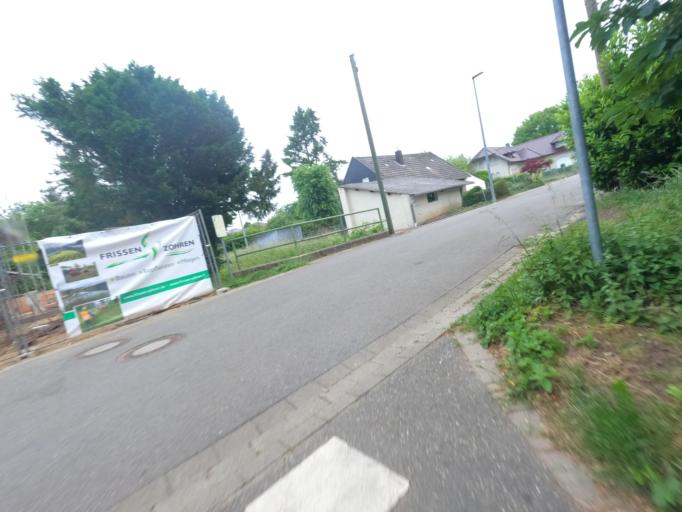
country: NL
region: Limburg
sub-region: Gemeente Roerdalen
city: Vlodrop
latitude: 51.1222
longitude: 6.0994
